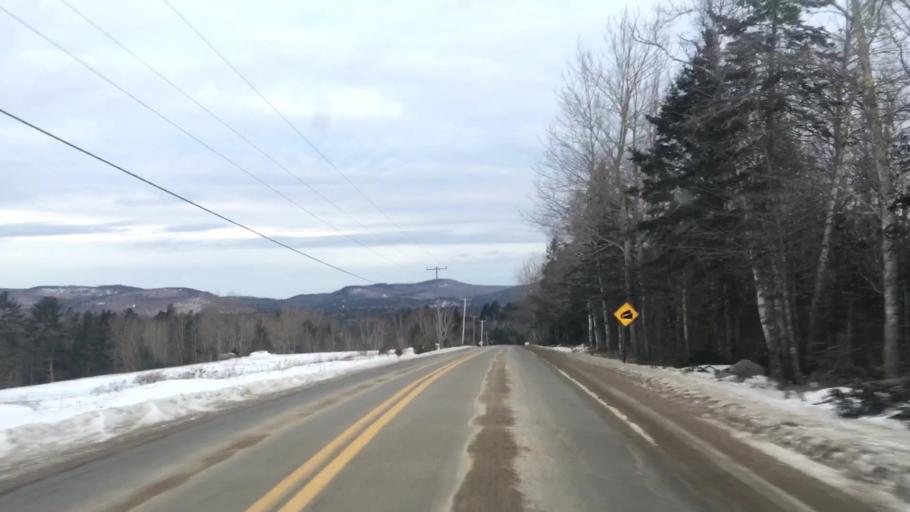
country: US
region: Maine
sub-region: Hancock County
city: Franklin
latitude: 44.8452
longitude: -68.3278
